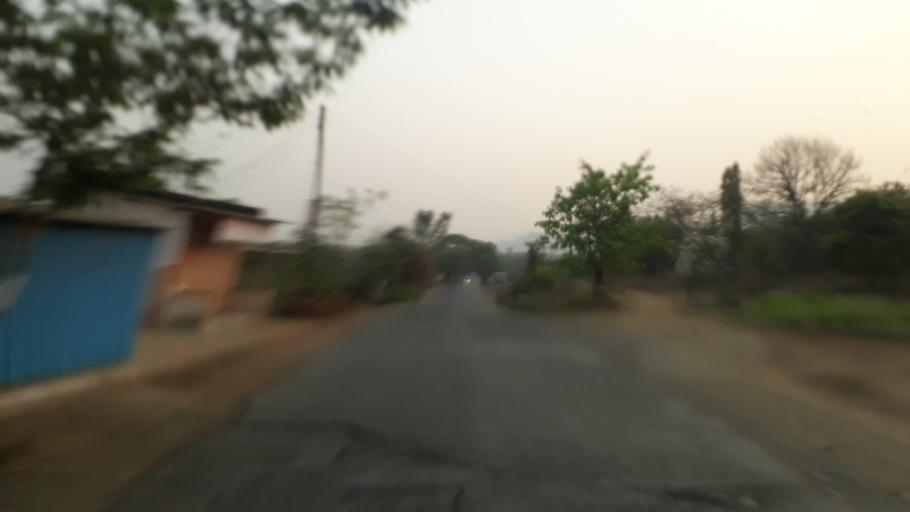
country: IN
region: Maharashtra
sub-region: Raigarh
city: Neral
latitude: 19.0465
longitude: 73.3322
